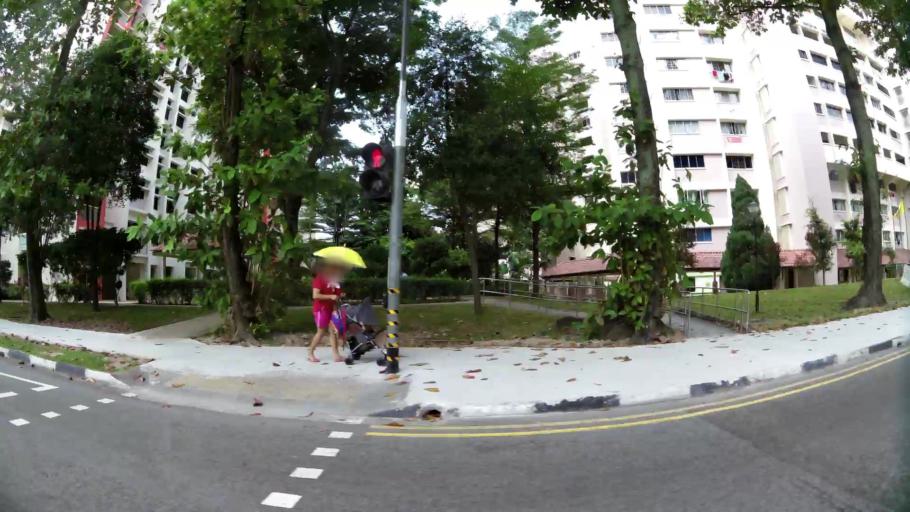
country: MY
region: Johor
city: Johor Bahru
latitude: 1.3480
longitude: 103.7313
